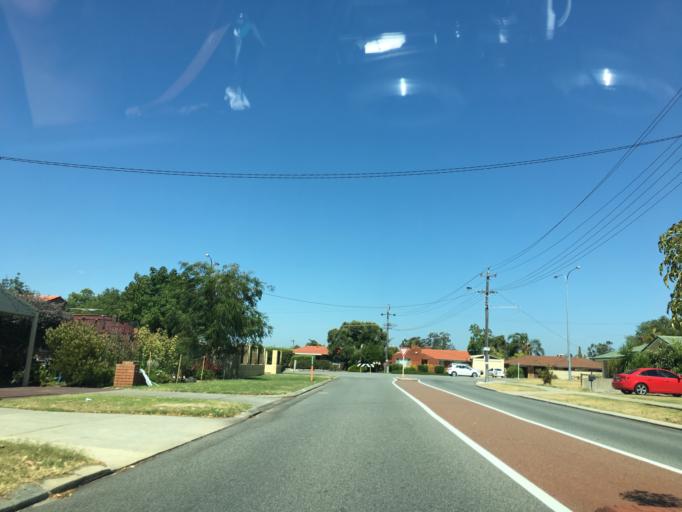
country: AU
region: Western Australia
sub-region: Canning
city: Willetton
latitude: -32.0478
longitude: 115.9033
